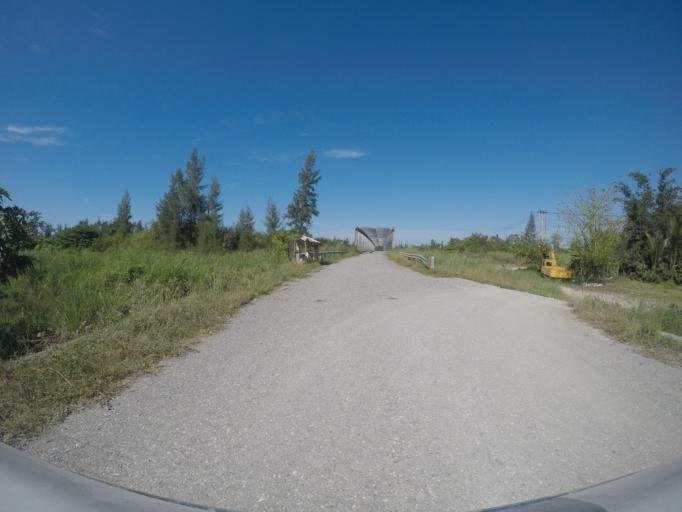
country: TL
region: Viqueque
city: Viqueque
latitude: -8.9457
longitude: 126.1117
